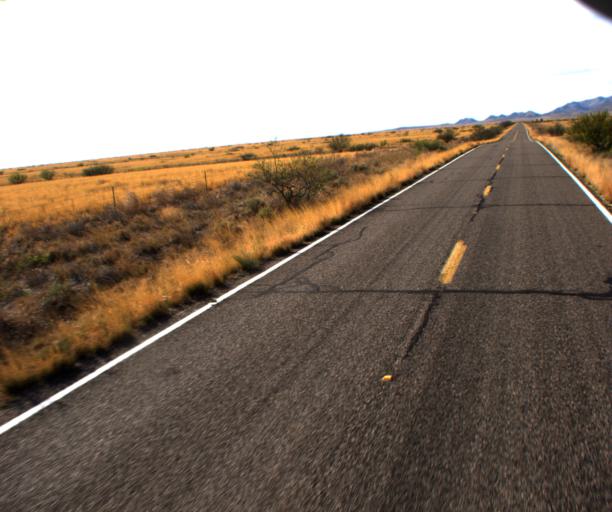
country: US
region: Arizona
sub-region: Cochise County
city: Willcox
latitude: 32.0832
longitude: -109.5239
